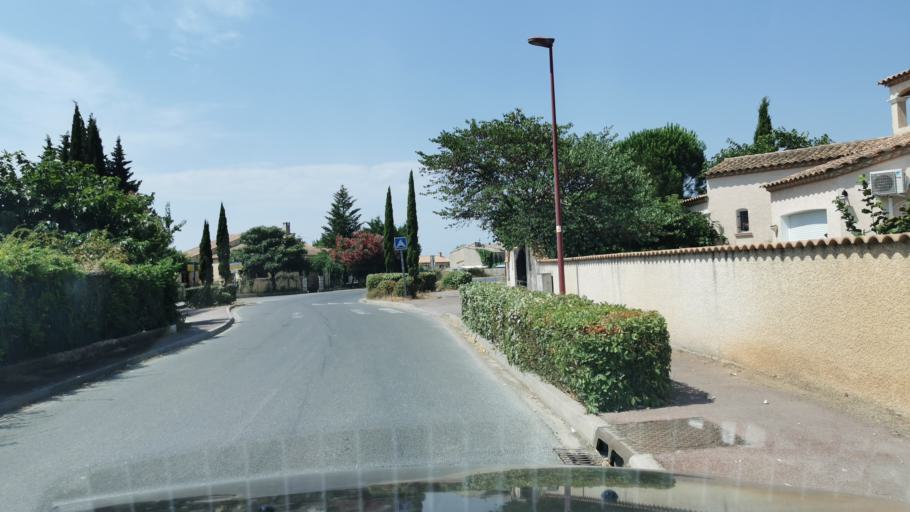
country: FR
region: Languedoc-Roussillon
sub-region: Departement de l'Aude
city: Ginestas
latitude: 43.2822
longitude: 2.8978
